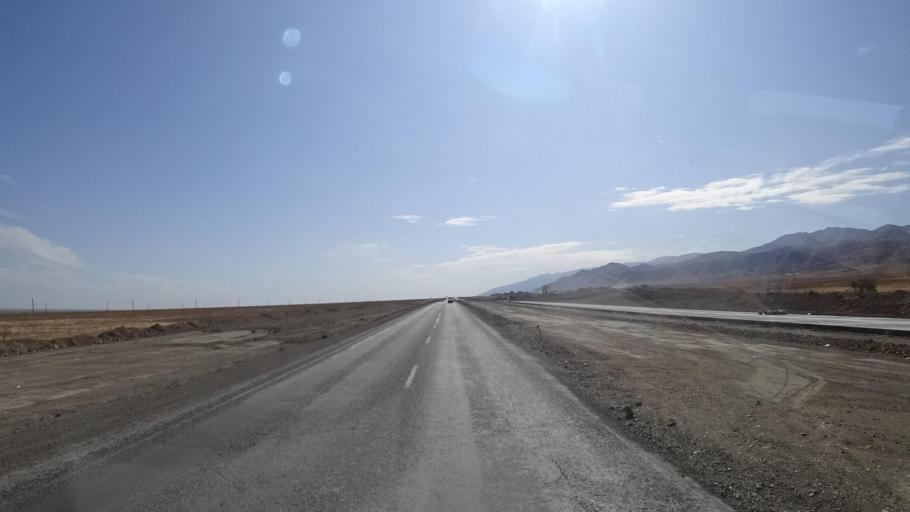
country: KG
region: Chuy
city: Ivanovka
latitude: 43.3952
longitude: 75.1293
